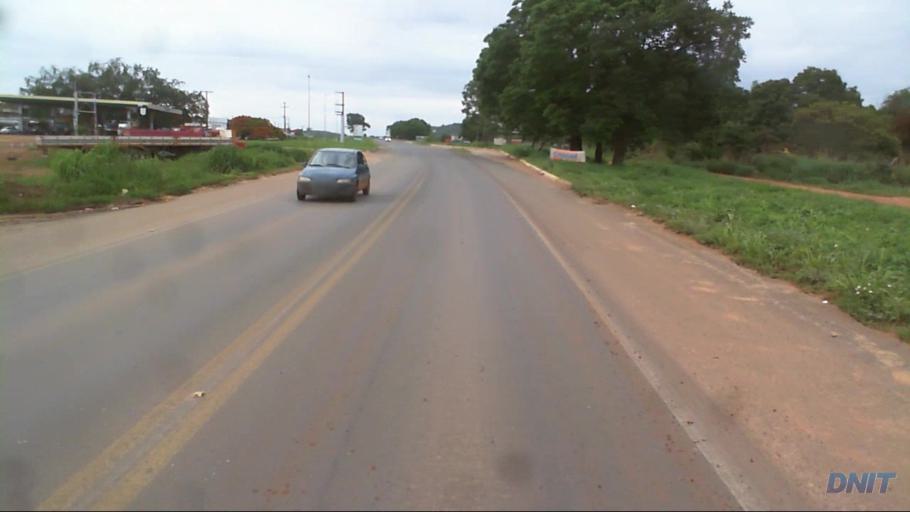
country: BR
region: Goias
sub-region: Uruacu
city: Uruacu
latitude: -14.5409
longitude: -49.1622
